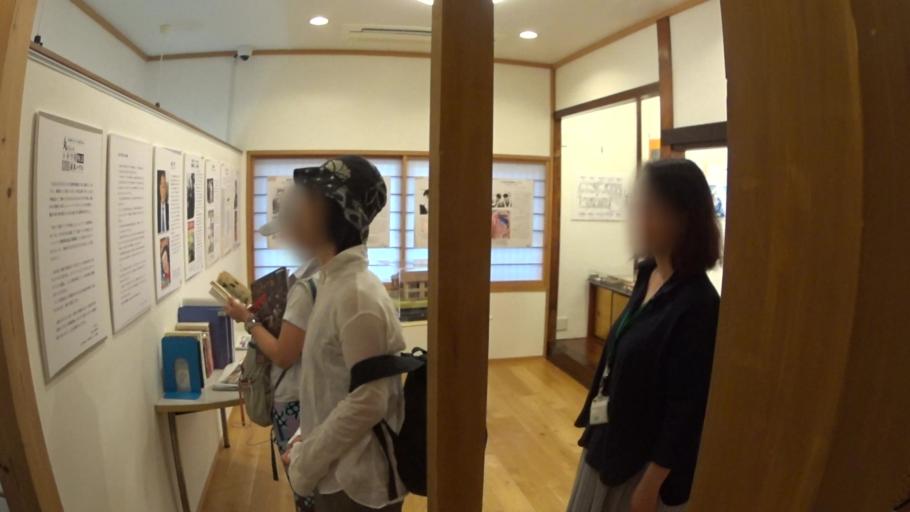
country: JP
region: Tokyo
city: Tokyo
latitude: 35.7244
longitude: 139.6873
